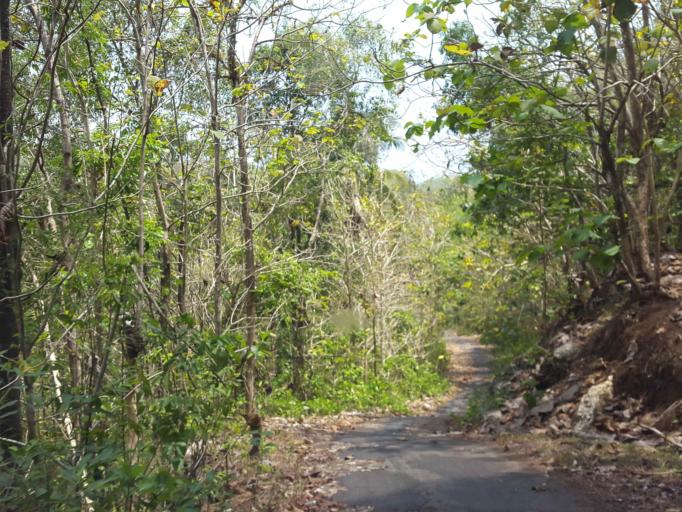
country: ID
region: East Java
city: Sudimoro
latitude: -8.2494
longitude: 111.2098
